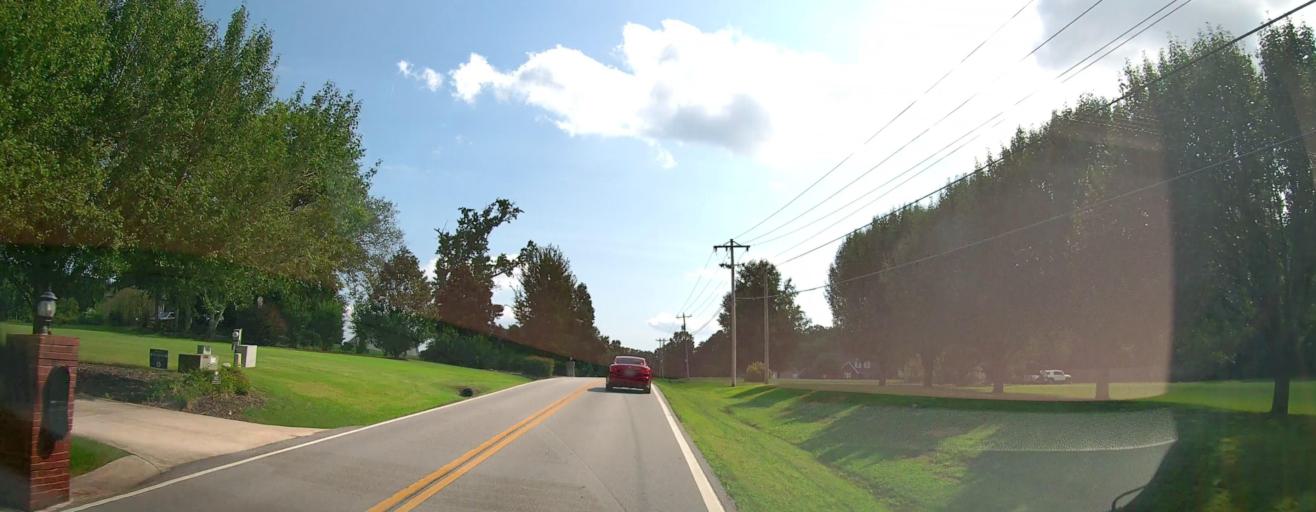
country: US
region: Georgia
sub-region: Catoosa County
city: Ringgold
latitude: 34.9260
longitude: -85.0848
